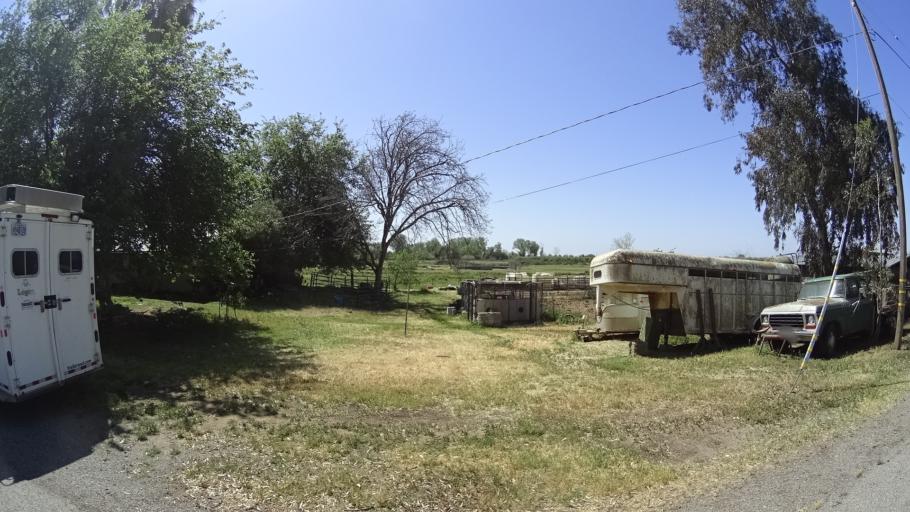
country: US
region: California
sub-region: Glenn County
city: Orland
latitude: 39.7652
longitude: -122.1635
